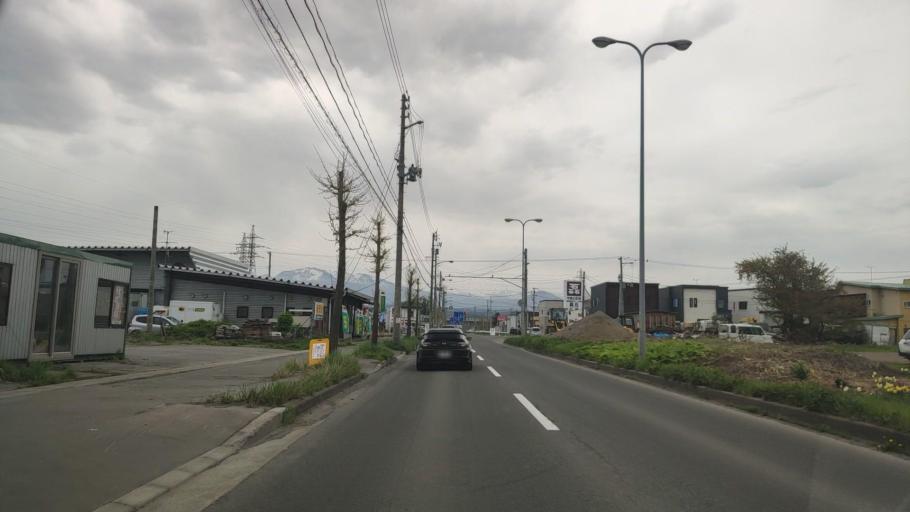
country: JP
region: Aomori
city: Aomori Shi
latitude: 40.8029
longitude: 140.7819
